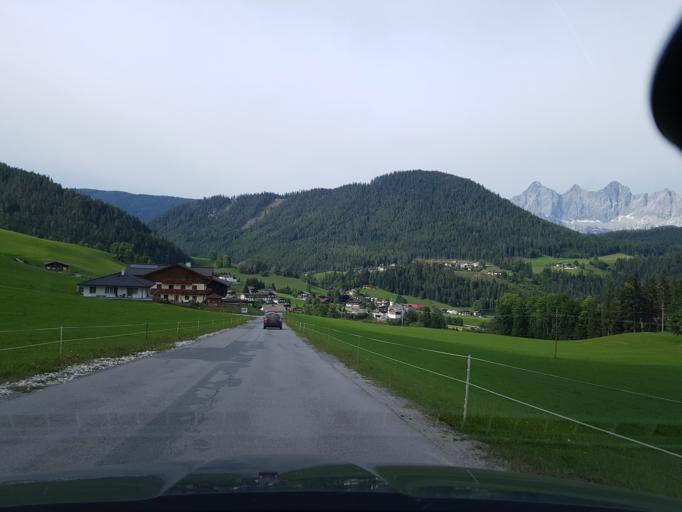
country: AT
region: Salzburg
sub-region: Politischer Bezirk Sankt Johann im Pongau
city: Forstau
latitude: 47.3709
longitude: 13.5519
